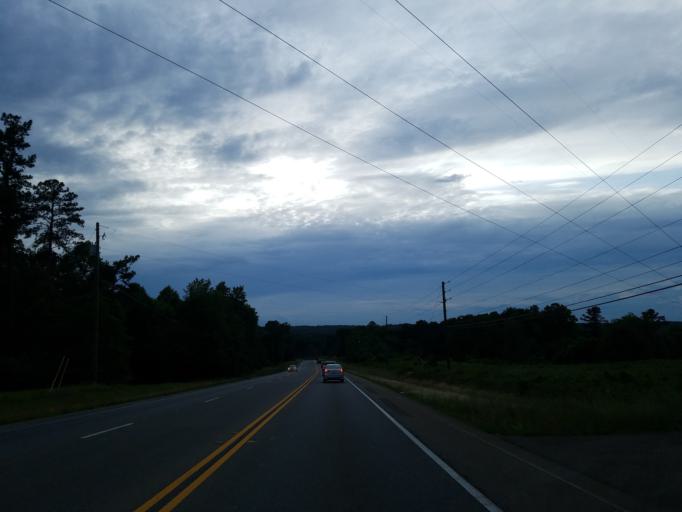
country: US
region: Georgia
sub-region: Cherokee County
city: Ball Ground
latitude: 34.2480
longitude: -84.3066
